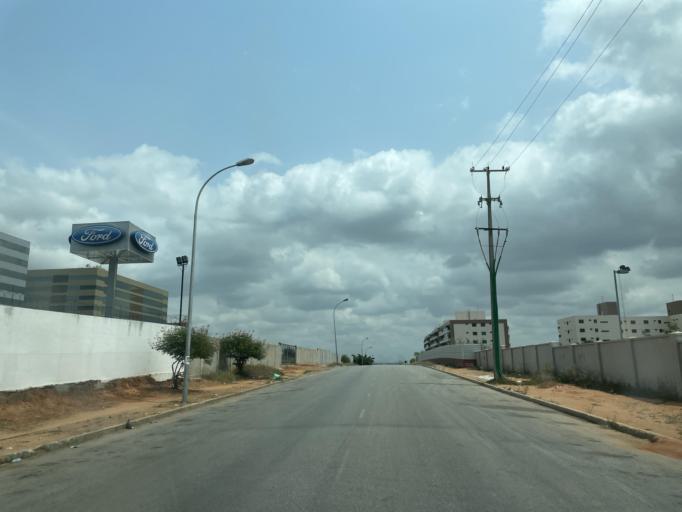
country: AO
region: Luanda
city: Luanda
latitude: -8.9235
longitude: 13.1876
